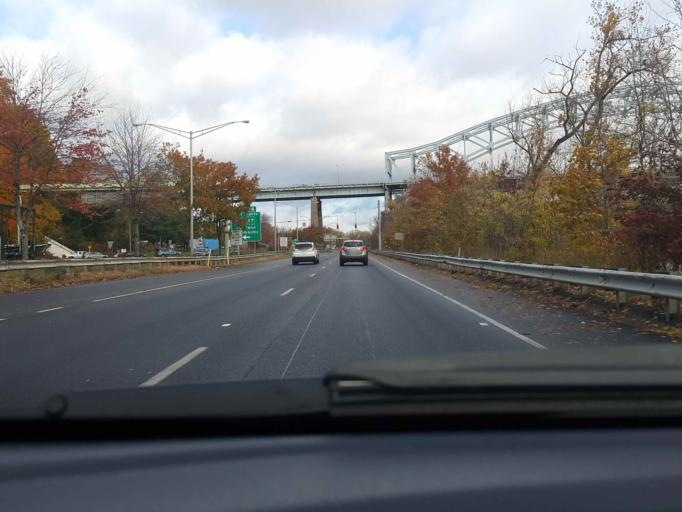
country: US
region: Connecticut
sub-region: Middlesex County
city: Middletown
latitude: 41.5666
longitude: -72.6498
